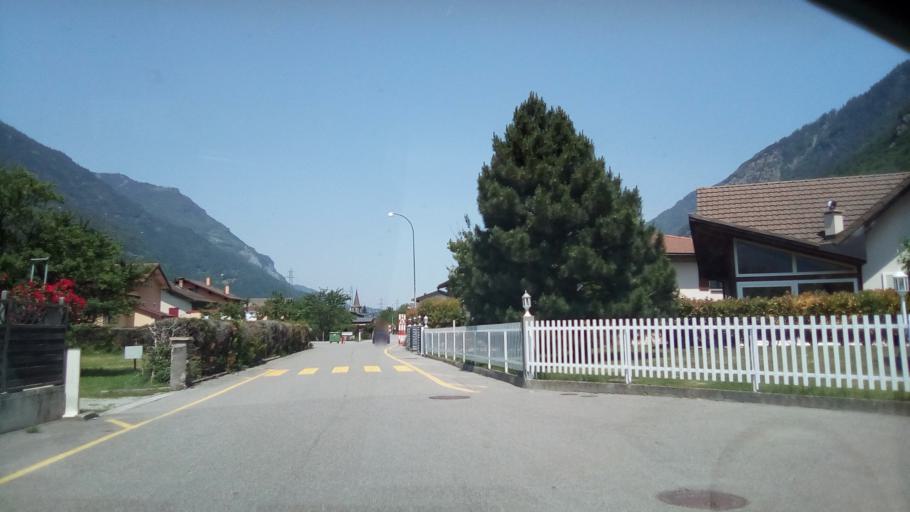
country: CH
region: Valais
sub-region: Saint-Maurice District
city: Vernayaz
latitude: 46.1449
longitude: 7.0447
